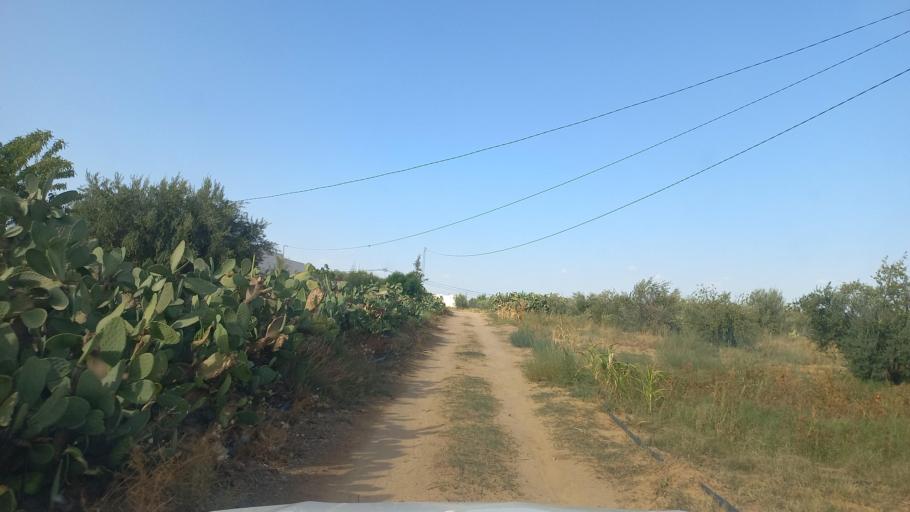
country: TN
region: Al Qasrayn
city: Kasserine
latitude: 35.2569
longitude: 9.0250
